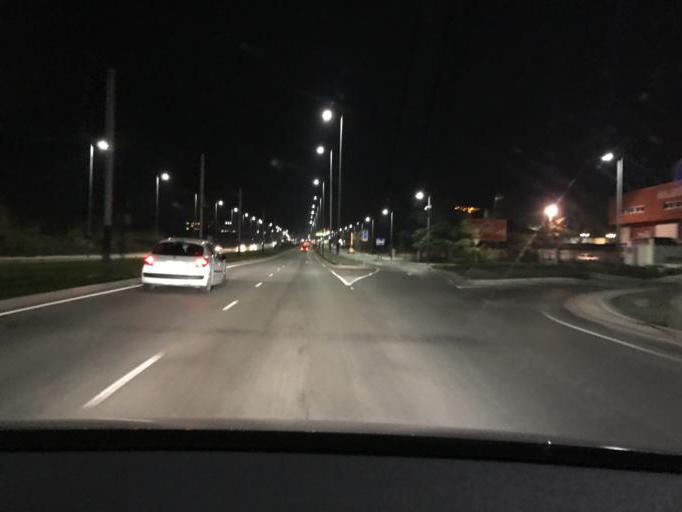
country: ES
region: Andalusia
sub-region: Provincia de Jaen
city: Jaen
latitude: 37.8024
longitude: -3.7778
